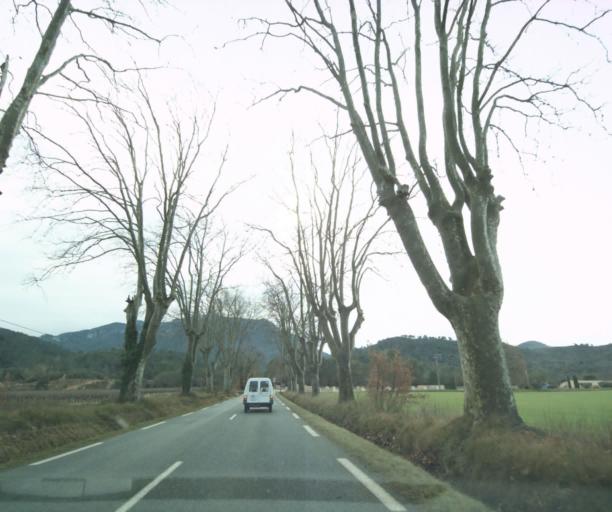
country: FR
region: Provence-Alpes-Cote d'Azur
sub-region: Departement du Var
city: La Roquebrussanne
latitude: 43.3923
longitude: 5.9753
